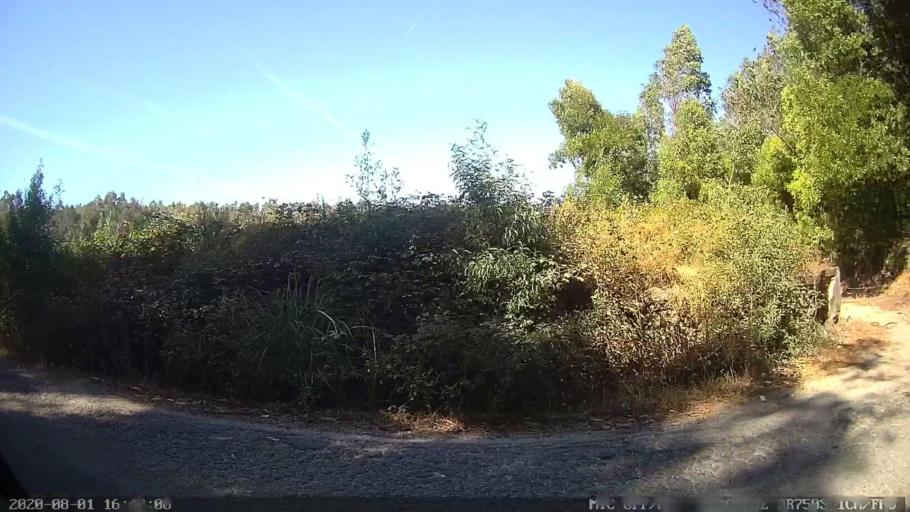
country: PT
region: Porto
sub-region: Maia
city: Anta
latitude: 41.2938
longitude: -8.6164
